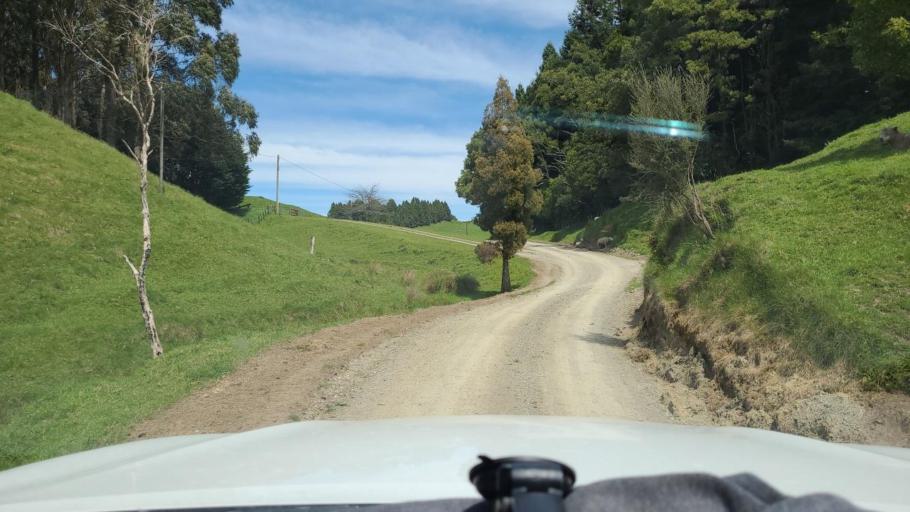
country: NZ
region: Hawke's Bay
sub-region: Wairoa District
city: Wairoa
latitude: -38.5642
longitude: 177.4808
